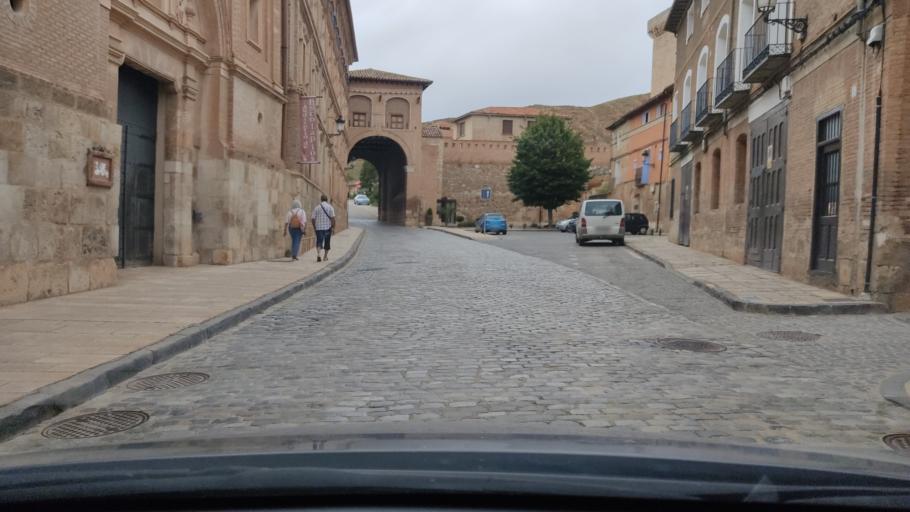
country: ES
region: Aragon
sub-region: Provincia de Zaragoza
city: Daroca
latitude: 41.1143
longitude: -1.4108
